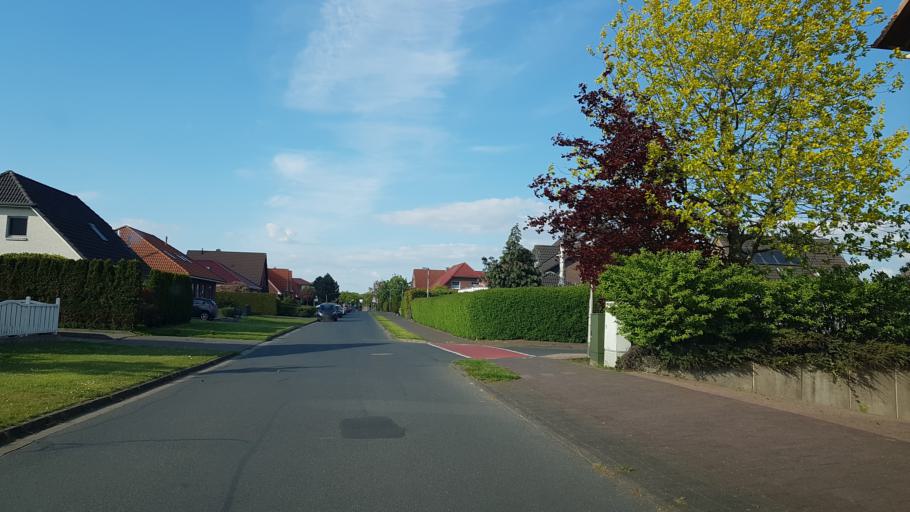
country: DE
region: Lower Saxony
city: Langen
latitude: 53.6051
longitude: 8.5874
